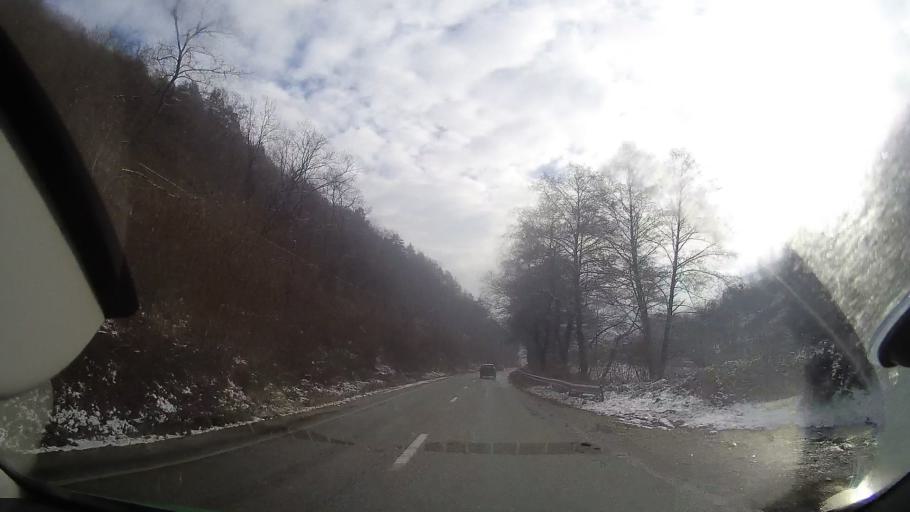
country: RO
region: Alba
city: Salciua de Sus
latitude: 46.3985
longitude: 23.3813
